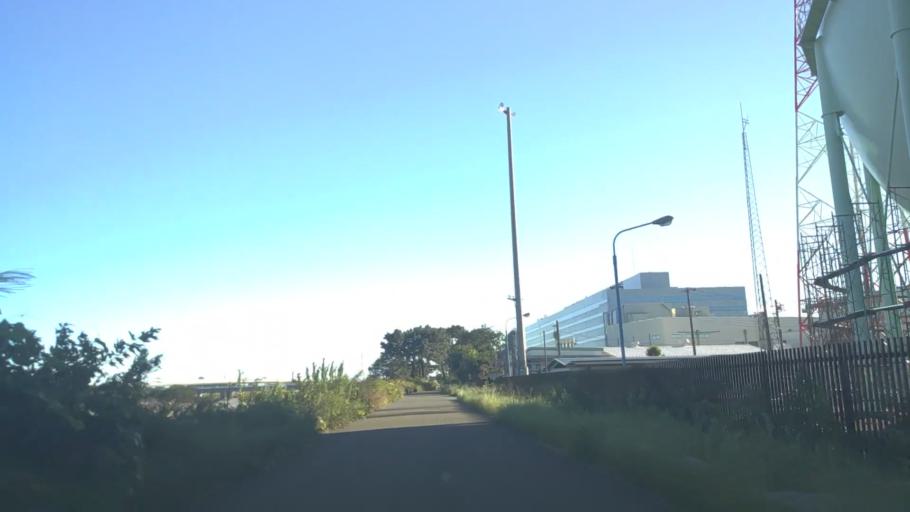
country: JP
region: Kanagawa
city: Atsugi
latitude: 35.4307
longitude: 139.3712
